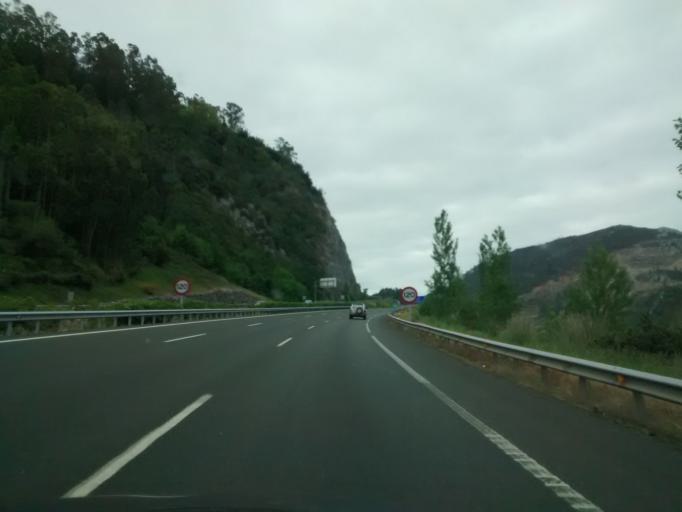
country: ES
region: Cantabria
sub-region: Provincia de Cantabria
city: Los Corrales de Buelna
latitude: 43.2876
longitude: -4.0806
